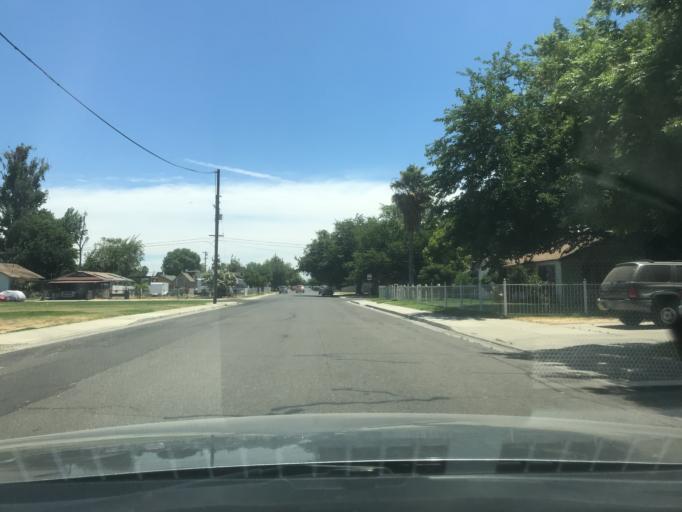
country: US
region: California
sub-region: Merced County
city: Atwater
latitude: 37.3463
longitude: -120.6049
